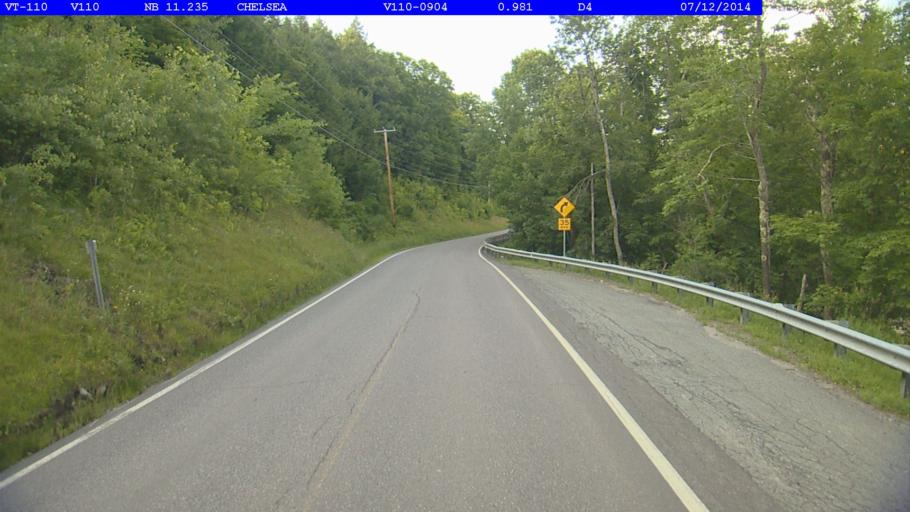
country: US
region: Vermont
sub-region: Orange County
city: Chelsea
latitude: 43.9648
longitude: -72.4631
